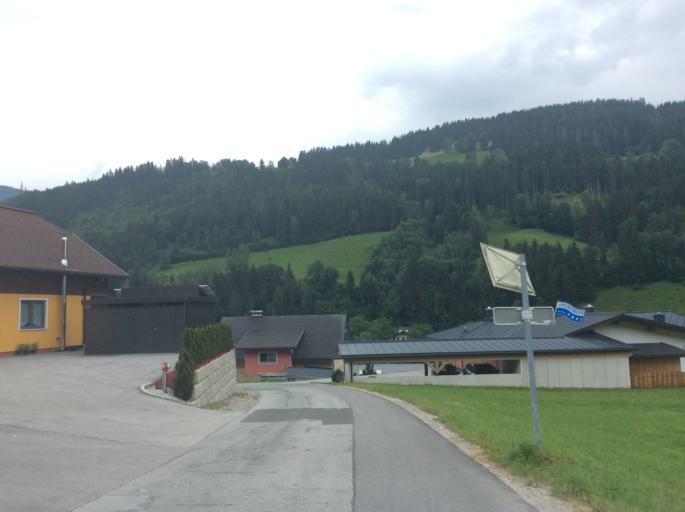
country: AT
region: Styria
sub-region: Politischer Bezirk Liezen
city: Schladming
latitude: 47.3912
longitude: 13.6541
